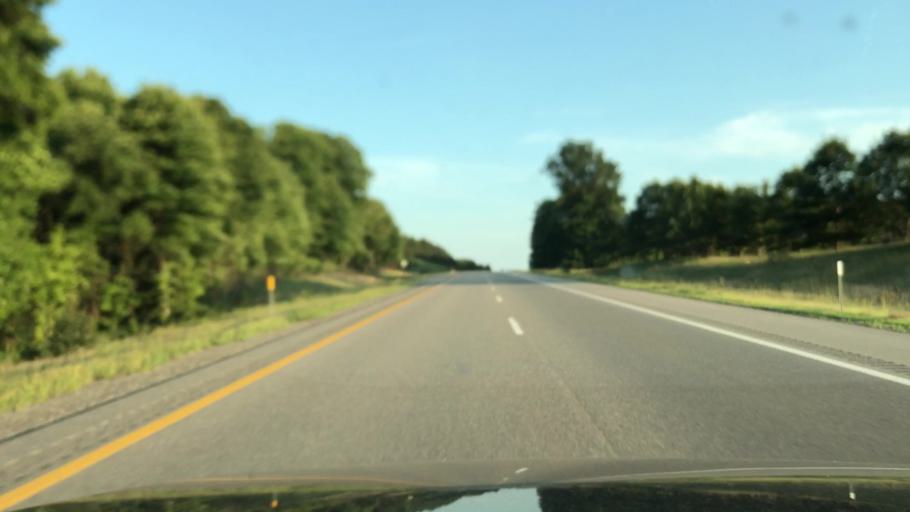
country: US
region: Michigan
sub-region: Osceola County
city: Reed City
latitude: 43.8541
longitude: -85.5335
